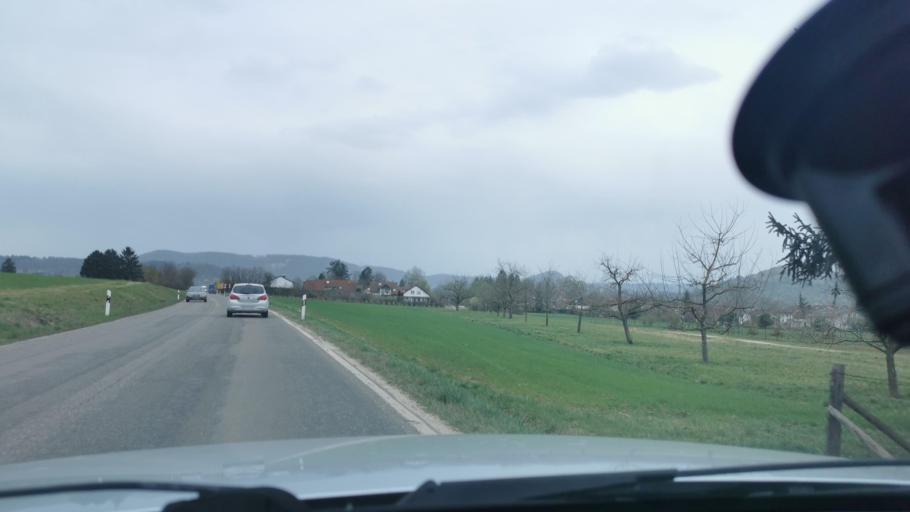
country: DE
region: Baden-Wuerttemberg
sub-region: Regierungsbezirk Stuttgart
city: Holzmaden
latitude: 48.6271
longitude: 9.5206
